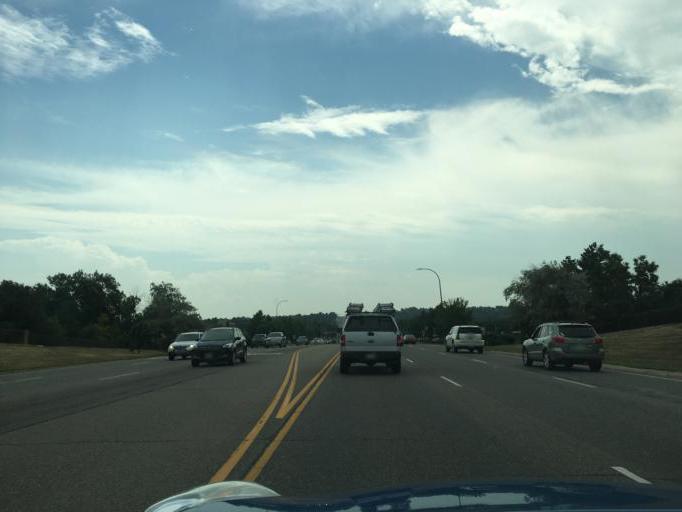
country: US
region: Colorado
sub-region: Jefferson County
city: Arvada
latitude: 39.8456
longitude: -105.0819
